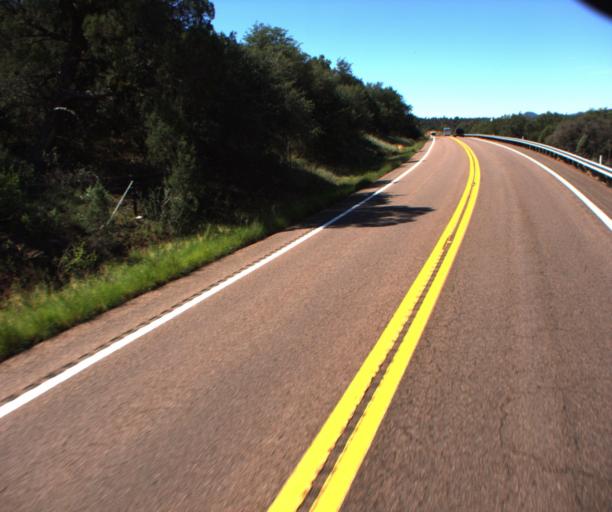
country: US
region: Arizona
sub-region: Navajo County
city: Cibecue
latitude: 33.9974
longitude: -110.2809
